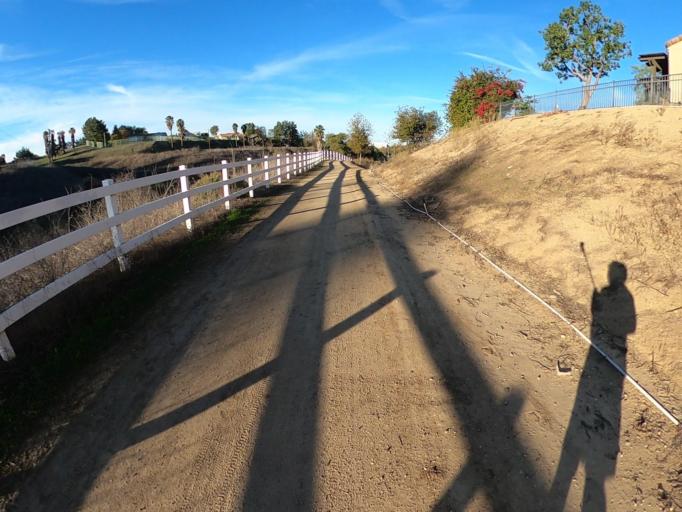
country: US
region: California
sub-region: Orange County
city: Brea
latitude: 33.8971
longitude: -117.9138
